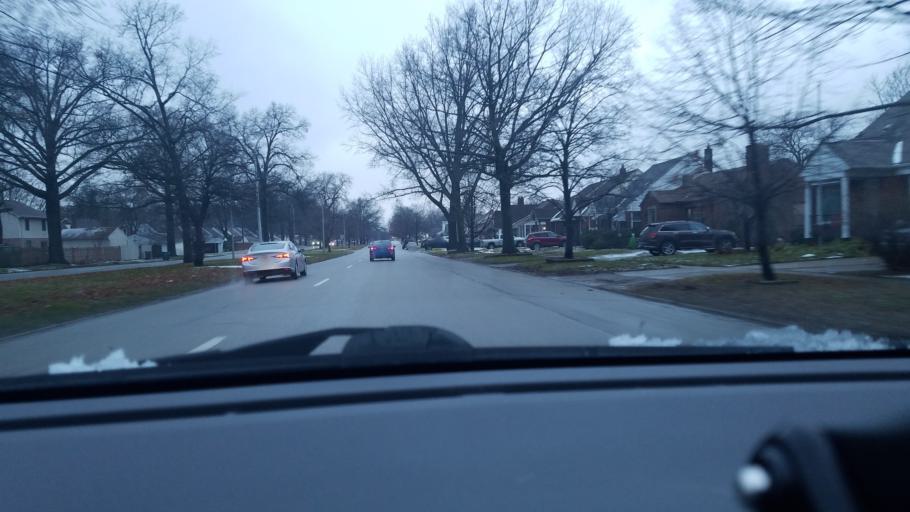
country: US
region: Michigan
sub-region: Wayne County
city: Dearborn Heights
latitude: 42.2929
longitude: -83.2509
